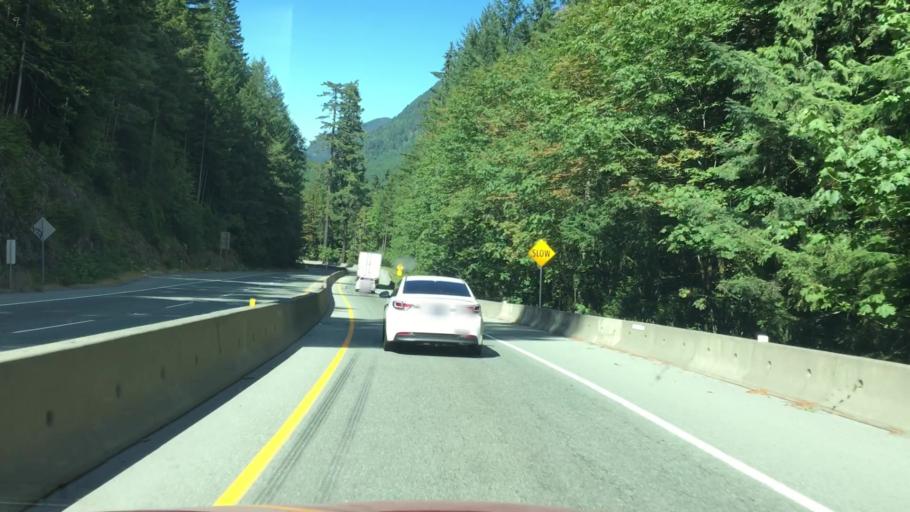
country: CA
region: British Columbia
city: Port Alberni
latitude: 49.2490
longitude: -124.6604
